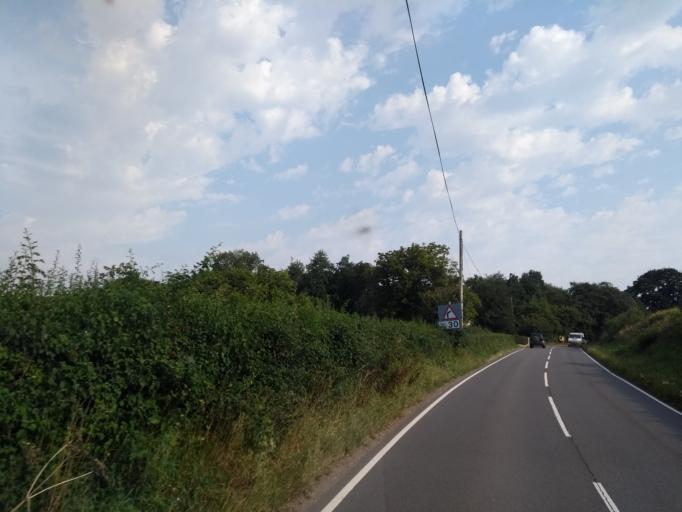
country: GB
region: England
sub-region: Devon
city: Axminster
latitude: 50.7571
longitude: -3.0246
